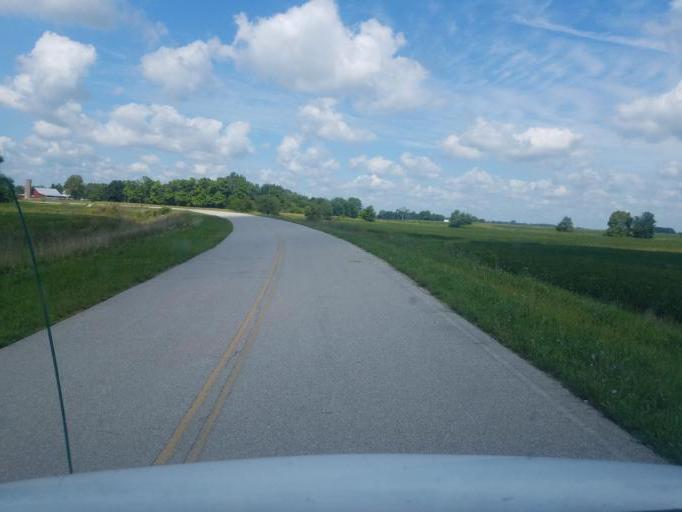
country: US
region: Ohio
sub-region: Marion County
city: Prospect
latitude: 40.4250
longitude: -83.1582
